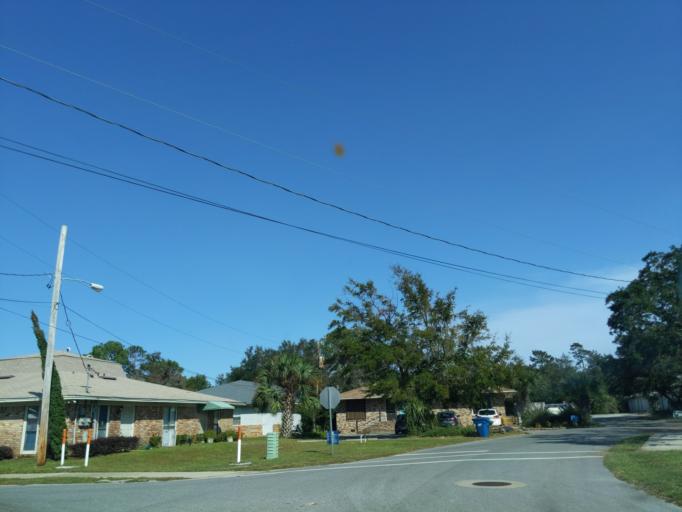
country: US
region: Florida
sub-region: Santa Rosa County
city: Gulf Breeze
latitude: 30.3635
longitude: -87.1714
